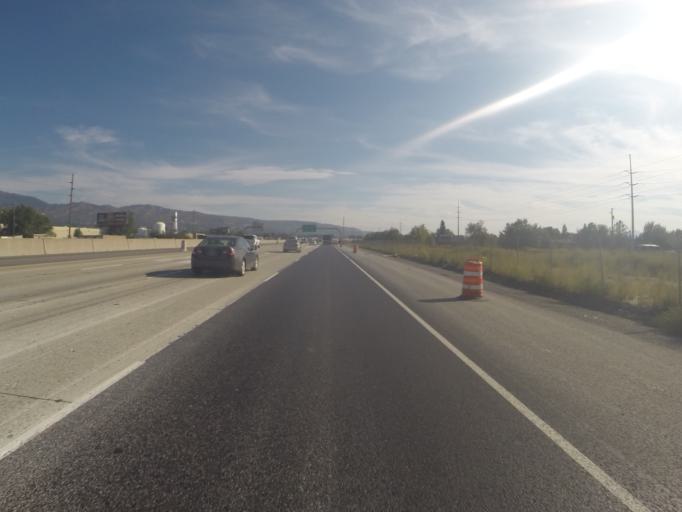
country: US
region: Utah
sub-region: Davis County
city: Centerville
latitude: 40.9130
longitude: -111.8916
